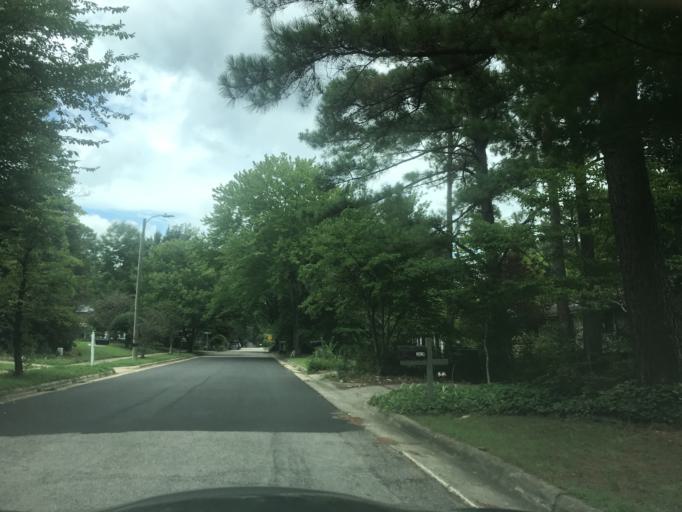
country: US
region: North Carolina
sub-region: Wake County
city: West Raleigh
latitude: 35.8913
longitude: -78.6136
